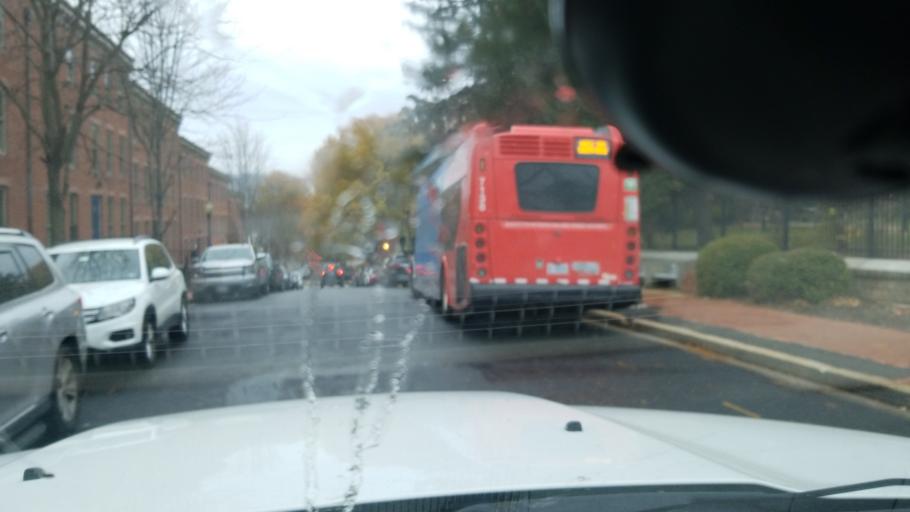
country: US
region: Washington, D.C.
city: Washington, D.C.
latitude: 38.9077
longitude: -77.0716
